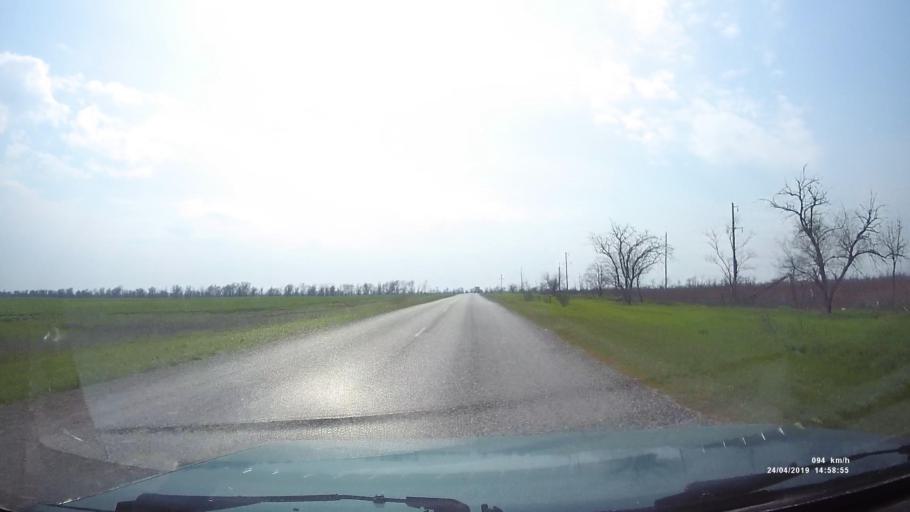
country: RU
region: Rostov
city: Remontnoye
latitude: 46.5670
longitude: 43.5885
